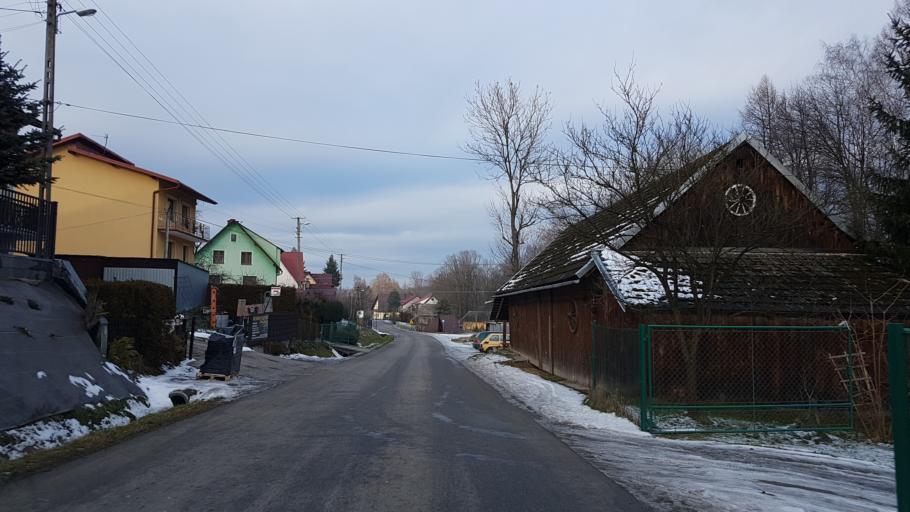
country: PL
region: Lesser Poland Voivodeship
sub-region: Powiat nowosadecki
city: Stary Sacz
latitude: 49.5201
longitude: 20.6085
